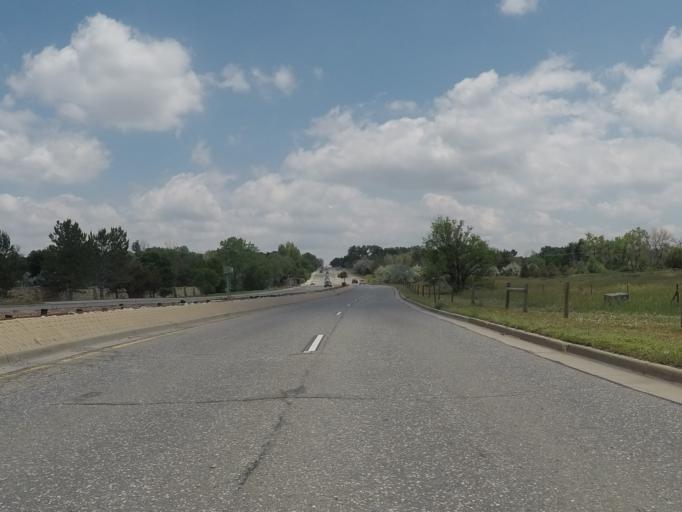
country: US
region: Colorado
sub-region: Arapahoe County
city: Greenwood Village
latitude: 39.6241
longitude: -104.9431
